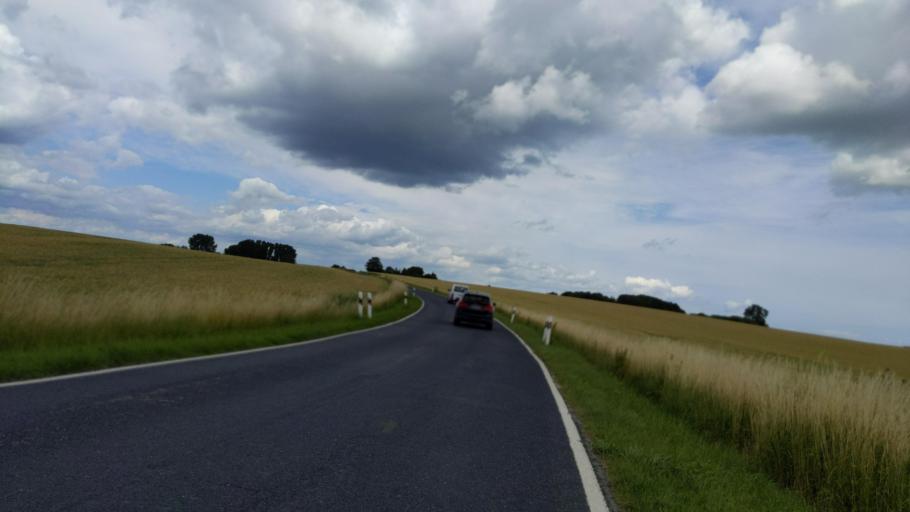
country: DE
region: Mecklenburg-Vorpommern
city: Dassow
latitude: 53.9473
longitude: 10.9737
